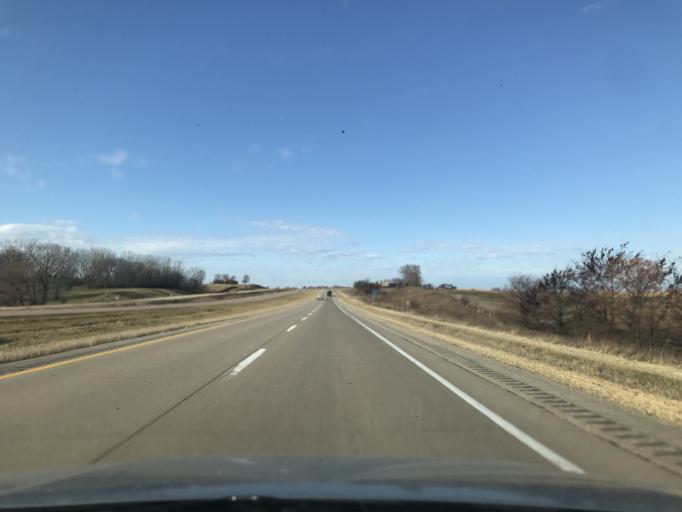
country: US
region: Iowa
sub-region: Jackson County
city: Maquoketa
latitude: 41.9699
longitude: -90.6464
